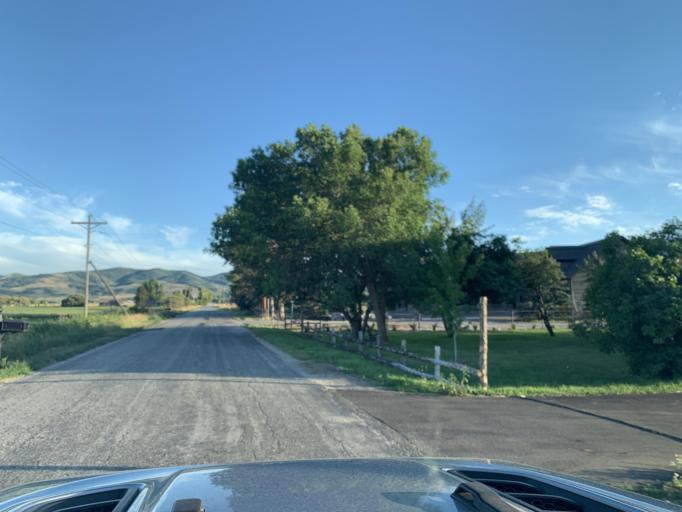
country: US
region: Utah
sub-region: Weber County
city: Wolf Creek
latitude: 41.2705
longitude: -111.7618
